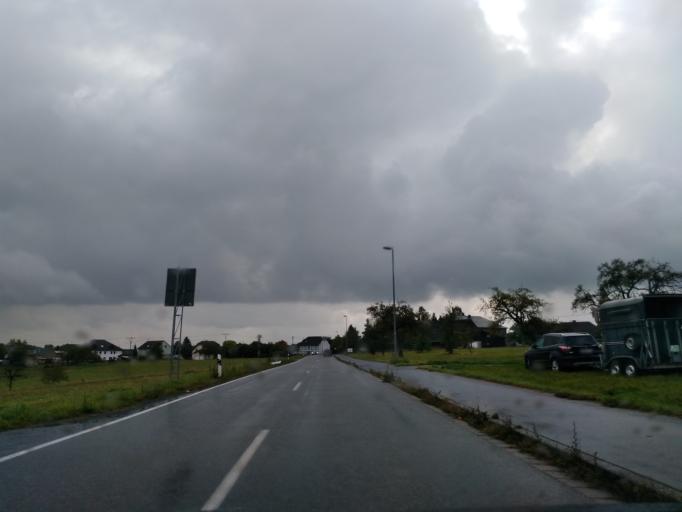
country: DE
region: Rheinland-Pfalz
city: Asbach
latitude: 50.6821
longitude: 7.4333
